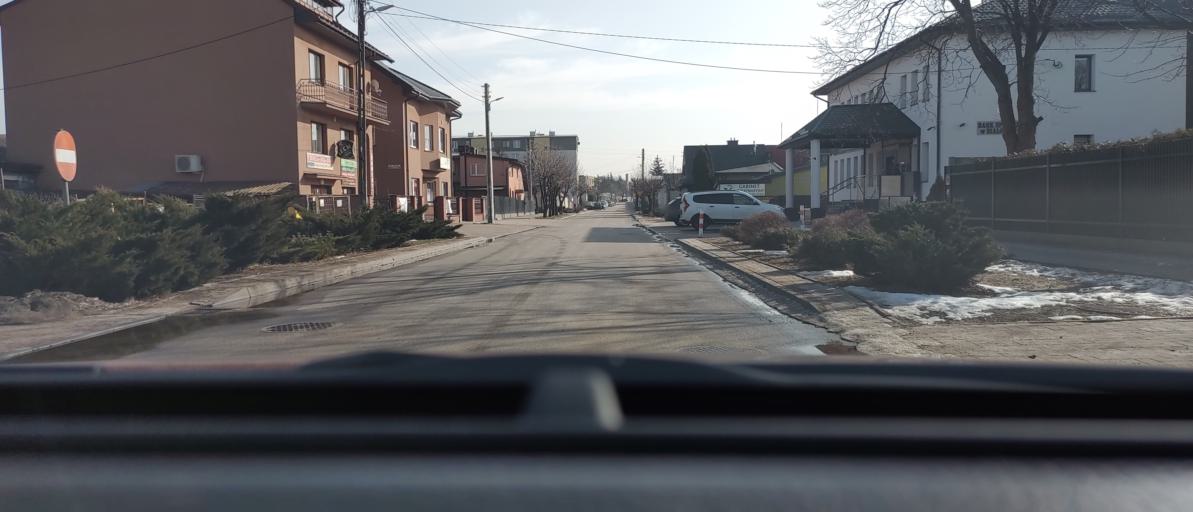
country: PL
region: Masovian Voivodeship
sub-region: Powiat bialobrzeski
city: Bialobrzegi
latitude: 51.6482
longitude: 20.9509
